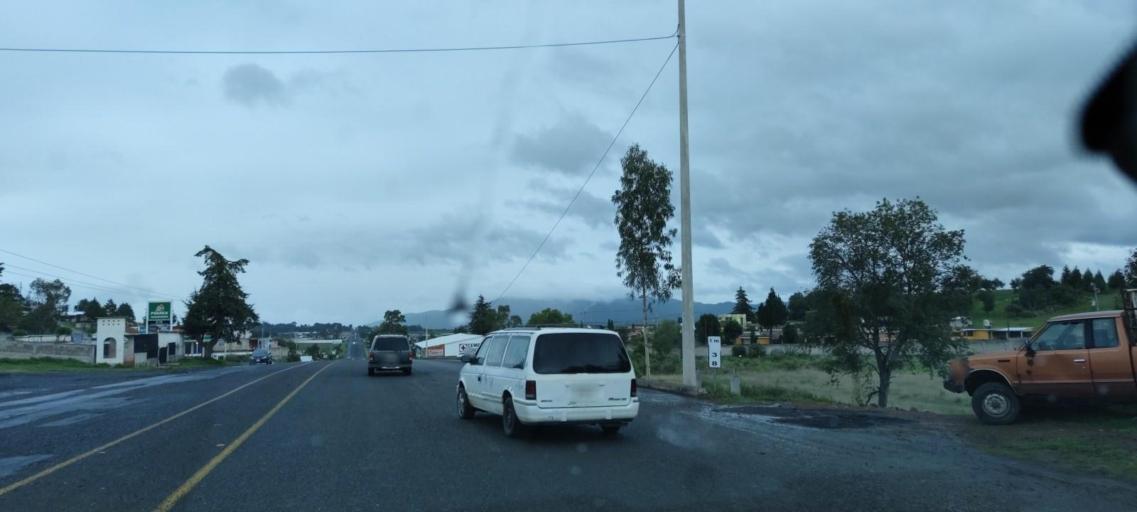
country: MX
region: Mexico
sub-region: Timilpan
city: Tercera Manzana de Zaragoza
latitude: 19.8820
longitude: -99.6607
